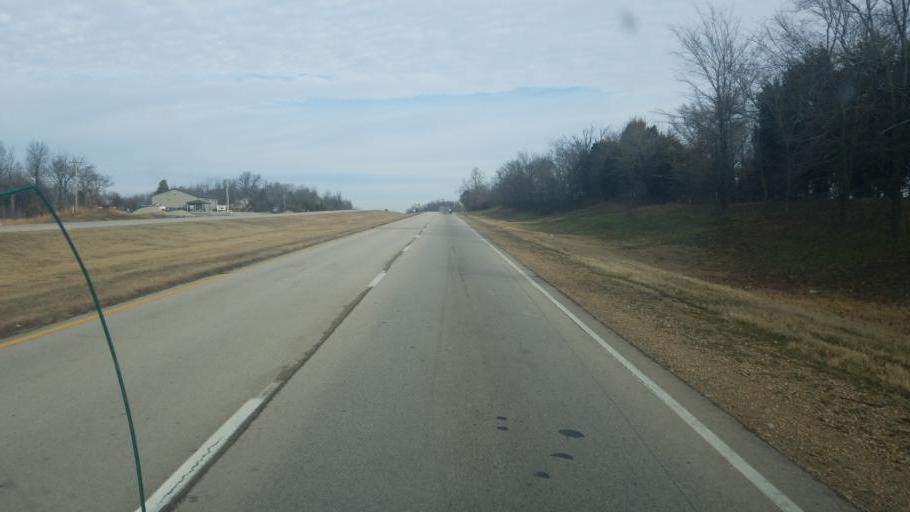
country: US
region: Missouri
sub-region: Stoddard County
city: Dexter
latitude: 36.8292
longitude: -89.9413
